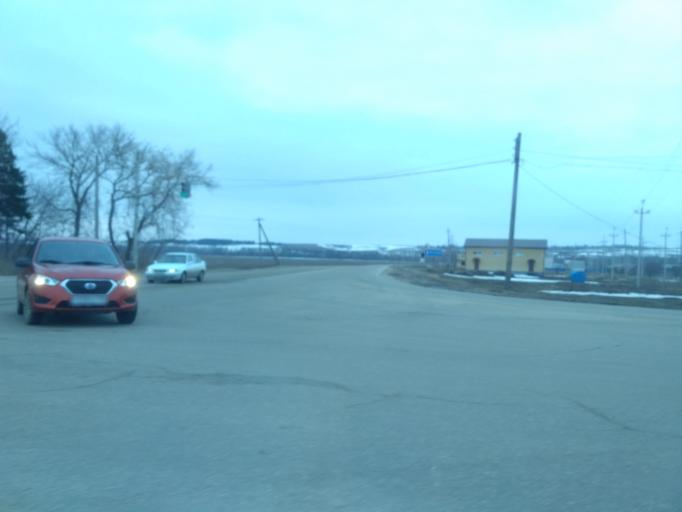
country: RU
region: Nizjnij Novgorod
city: Perevoz
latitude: 55.5979
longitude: 44.5610
